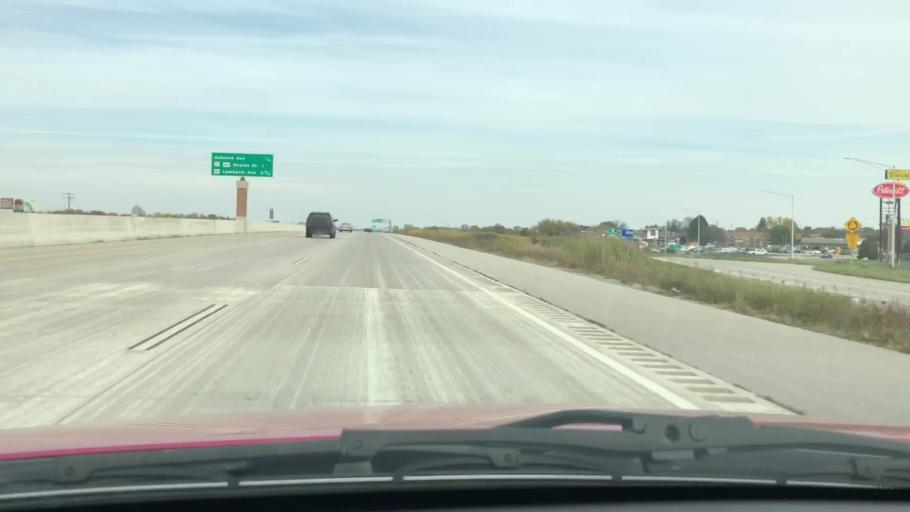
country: US
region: Wisconsin
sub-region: Brown County
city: De Pere
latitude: 44.4499
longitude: -88.0915
